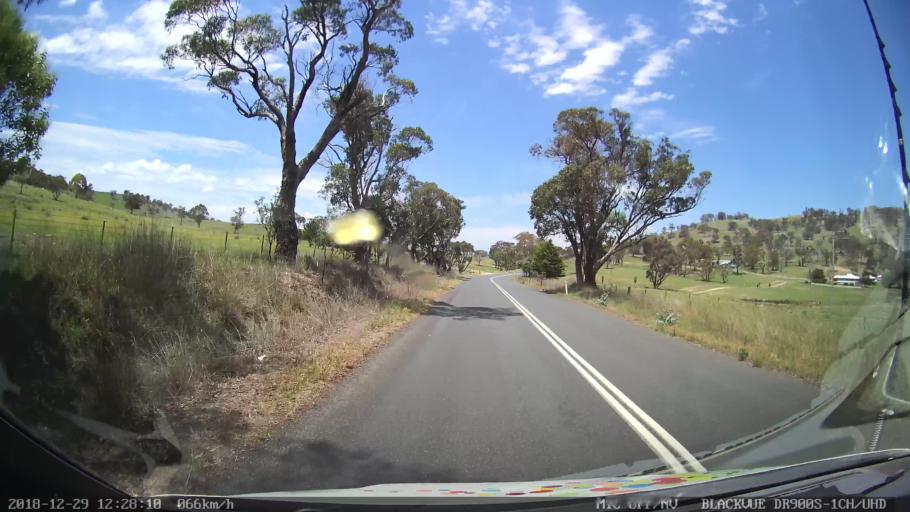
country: AU
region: Australian Capital Territory
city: Macarthur
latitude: -35.4837
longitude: 149.2255
